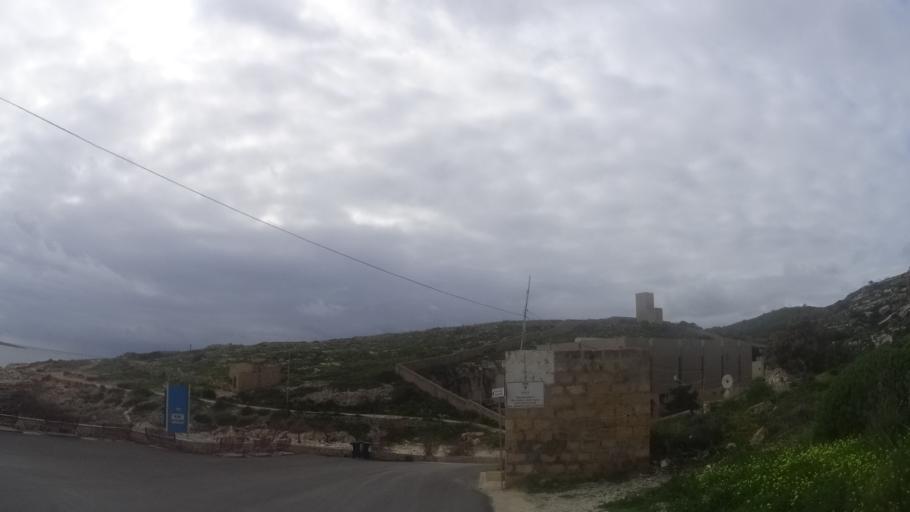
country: MT
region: Il-Qala
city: Qala
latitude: 36.0284
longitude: 14.3225
